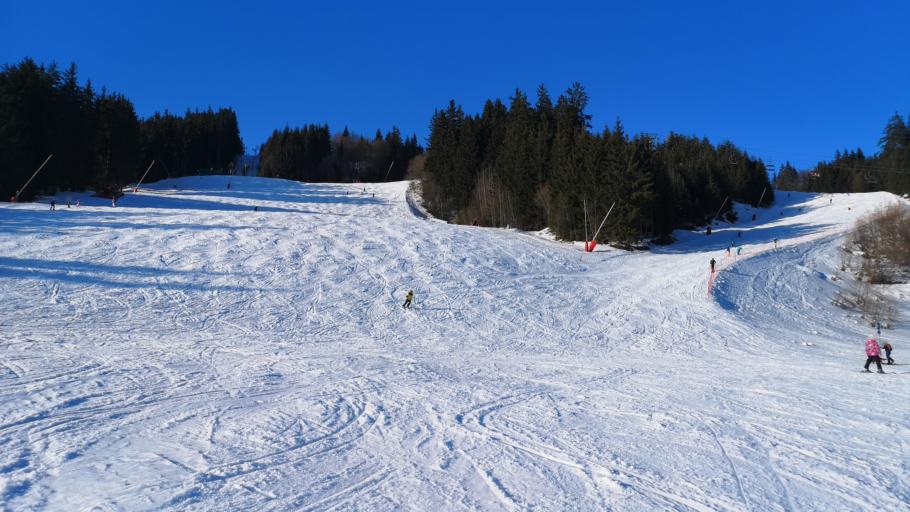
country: SK
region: Zilinsky
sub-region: Okres Dolny Kubin
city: Dolny Kubin
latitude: 49.2581
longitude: 19.2605
